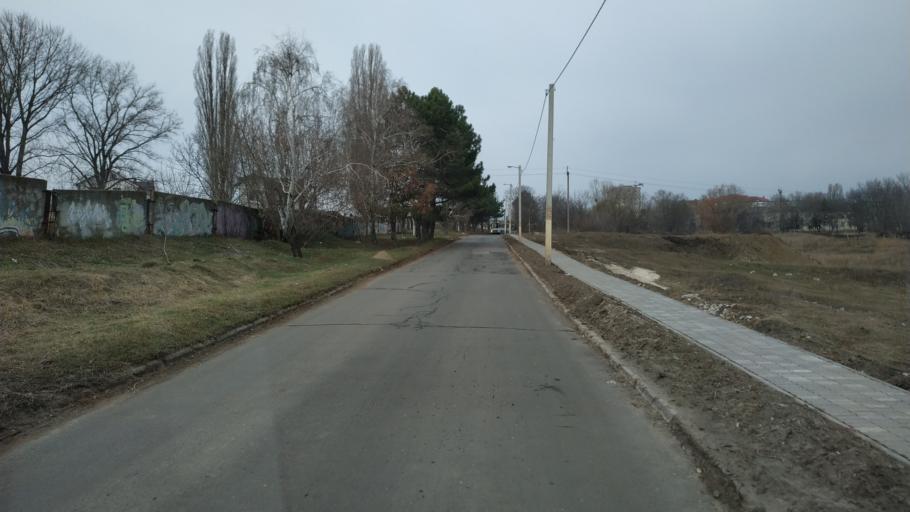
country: MD
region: Chisinau
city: Vatra
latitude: 47.0877
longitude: 28.7653
